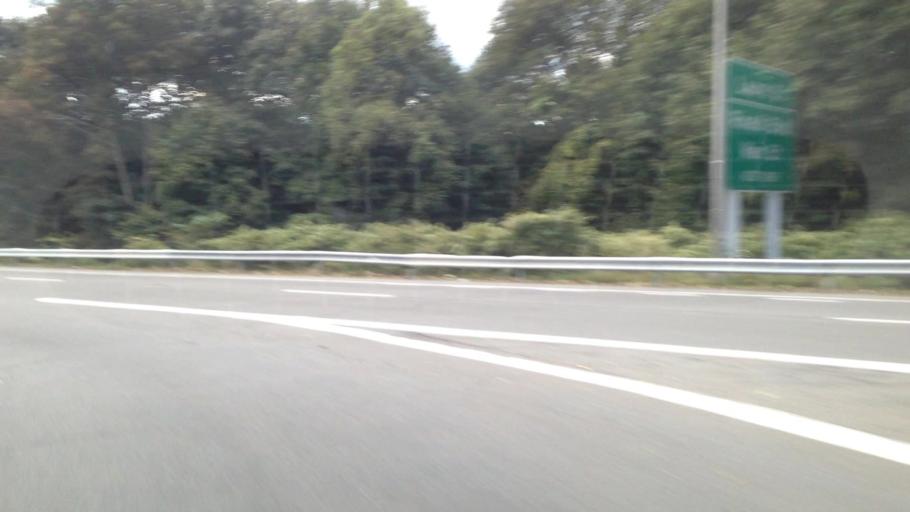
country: US
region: New York
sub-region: Dutchess County
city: Poughkeepsie
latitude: 41.7044
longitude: -73.9371
